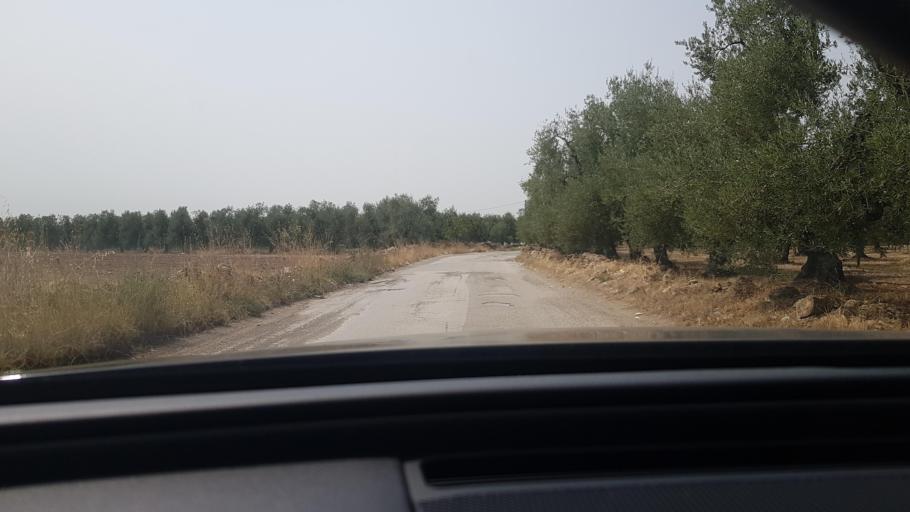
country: IT
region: Apulia
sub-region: Provincia di Barletta - Andria - Trani
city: Andria
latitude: 41.2182
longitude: 16.2613
